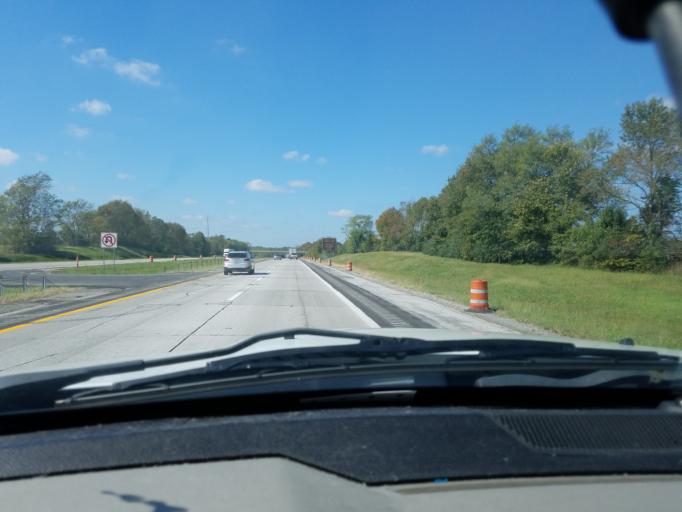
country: US
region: Kentucky
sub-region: Woodford County
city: Midway
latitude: 38.1717
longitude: -84.7761
